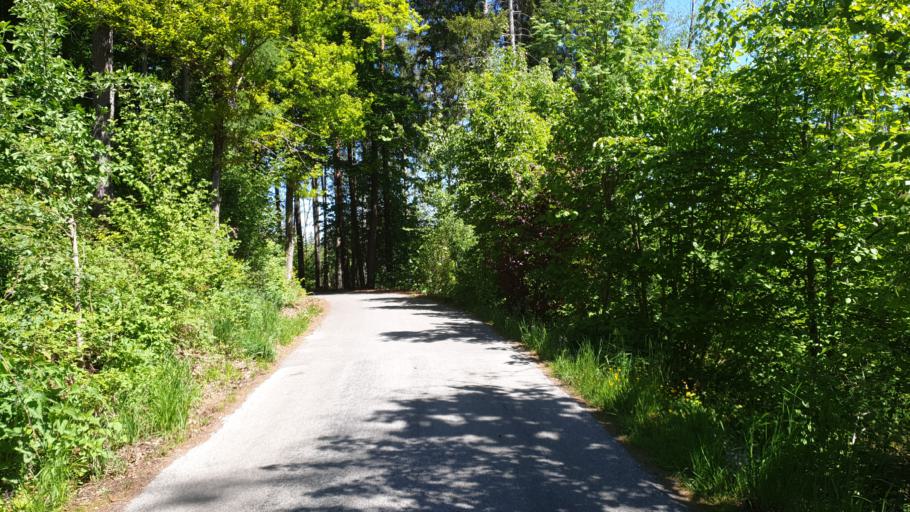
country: DE
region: Bavaria
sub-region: Upper Bavaria
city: Iffeldorf
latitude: 47.7744
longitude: 11.3072
